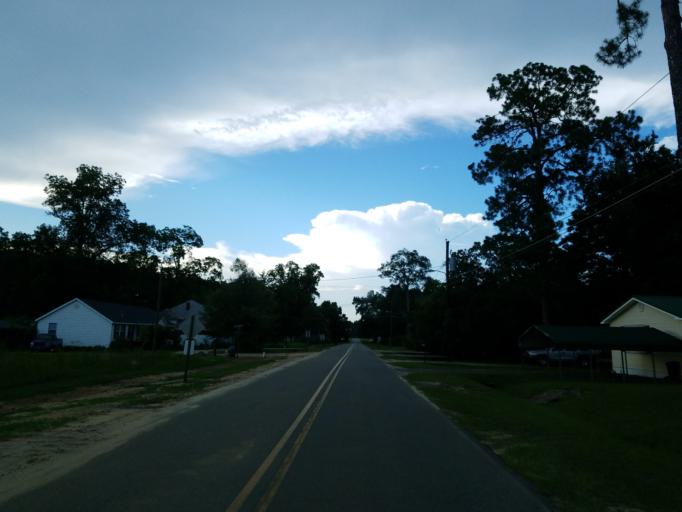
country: US
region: Georgia
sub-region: Cook County
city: Sparks
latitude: 31.2770
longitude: -83.4622
